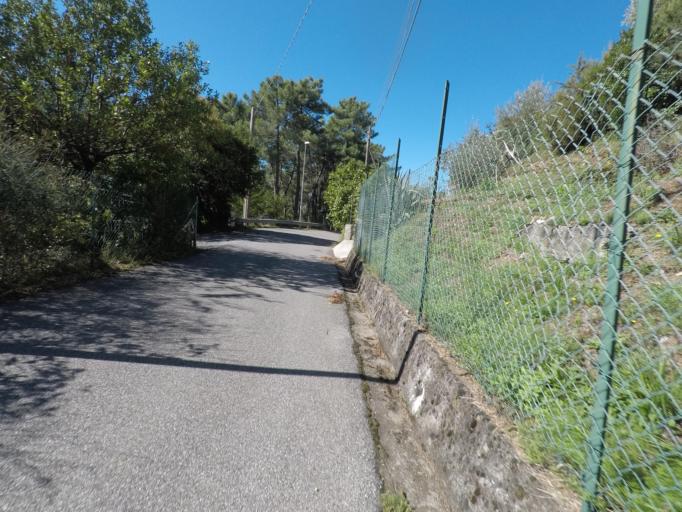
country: IT
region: Tuscany
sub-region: Provincia di Massa-Carrara
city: Montignoso
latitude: 44.0359
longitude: 10.1616
